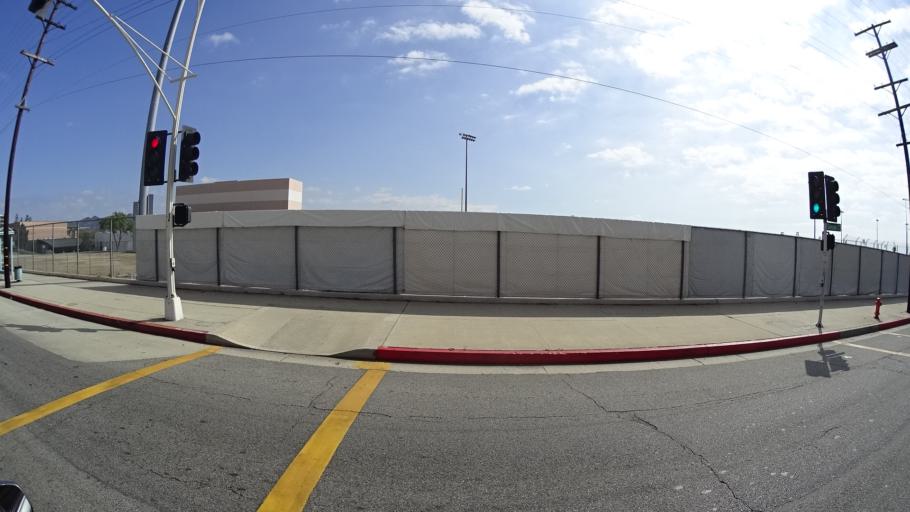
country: US
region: California
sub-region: Los Angeles County
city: Burbank
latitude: 34.1890
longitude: -118.3142
